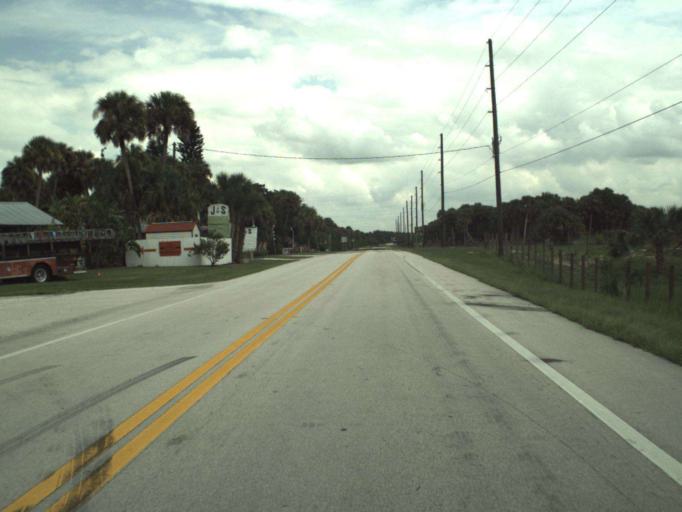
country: US
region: Florida
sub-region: Martin County
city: Indiantown
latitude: 27.0884
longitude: -80.6572
